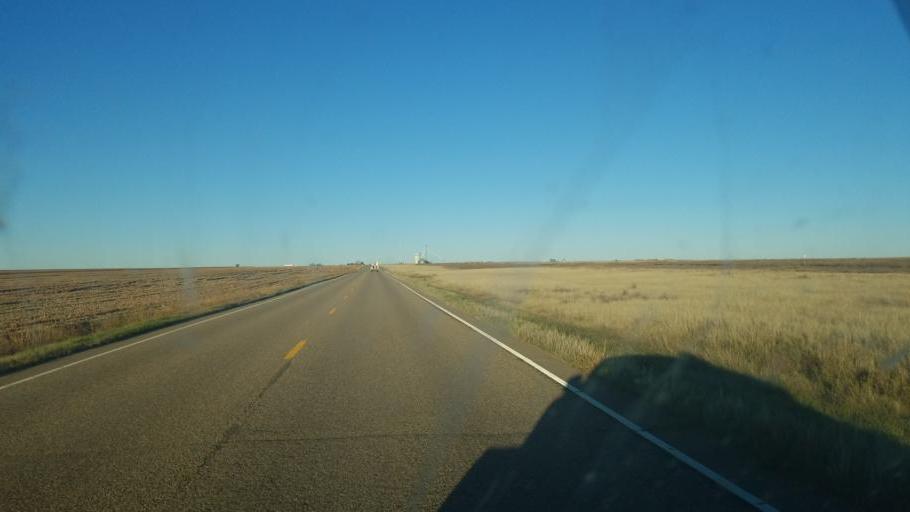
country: US
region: Colorado
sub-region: Cheyenne County
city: Cheyenne Wells
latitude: 38.8167
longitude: -102.5248
